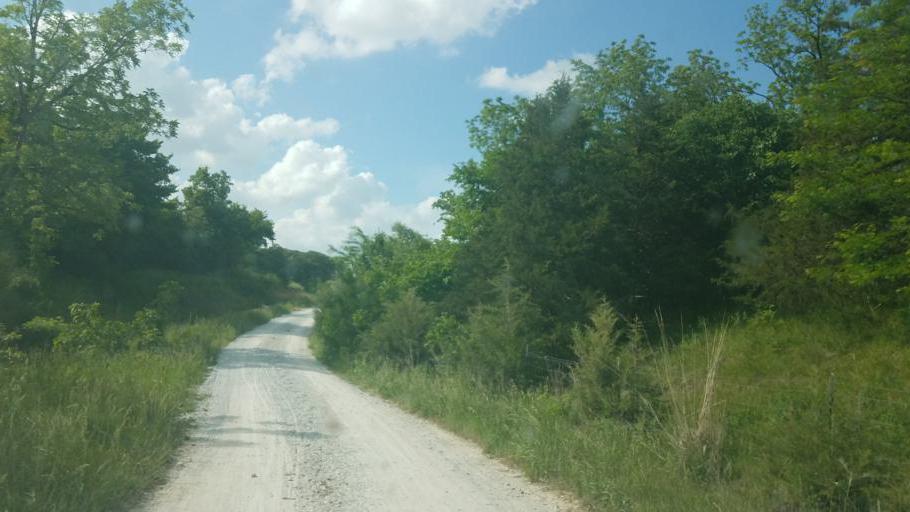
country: US
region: Missouri
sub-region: Cooper County
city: Boonville
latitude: 38.8514
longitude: -92.6453
